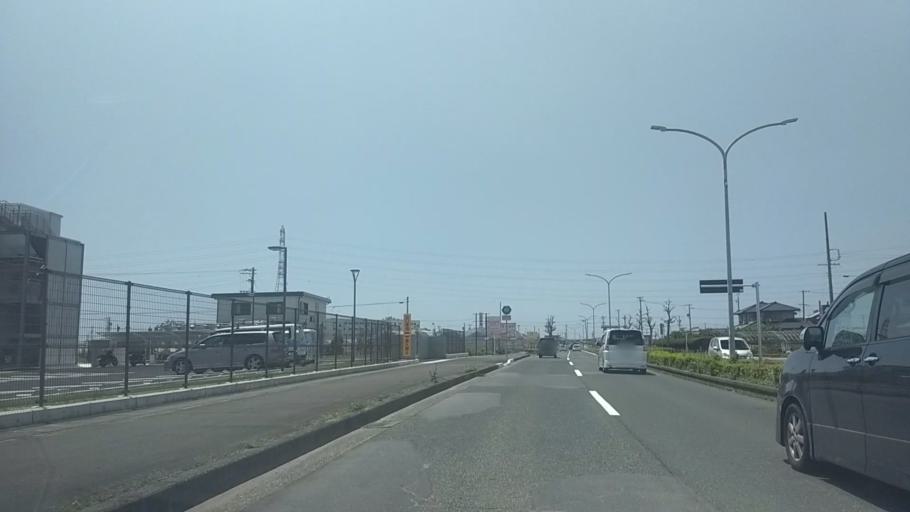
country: JP
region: Shizuoka
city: Hamamatsu
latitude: 34.7366
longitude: 137.6634
